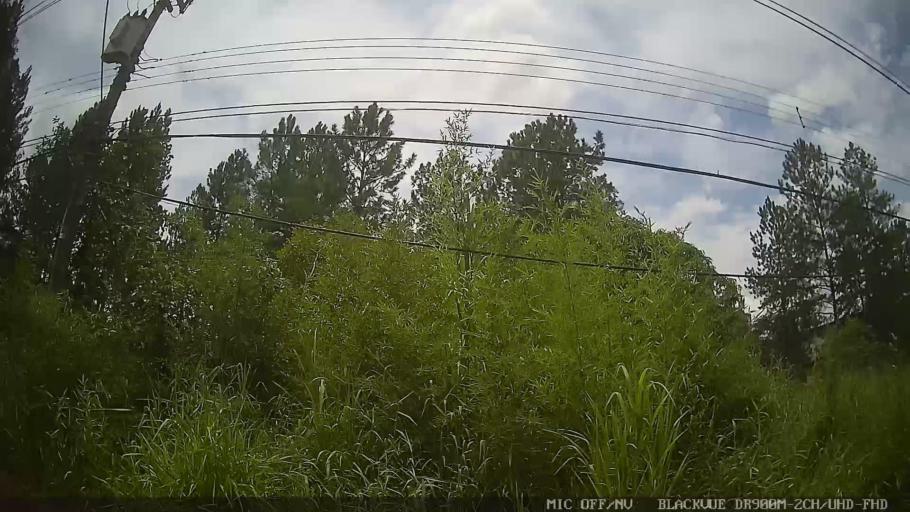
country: BR
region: Sao Paulo
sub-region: Santa Isabel
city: Santa Isabel
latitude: -23.3520
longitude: -46.2390
